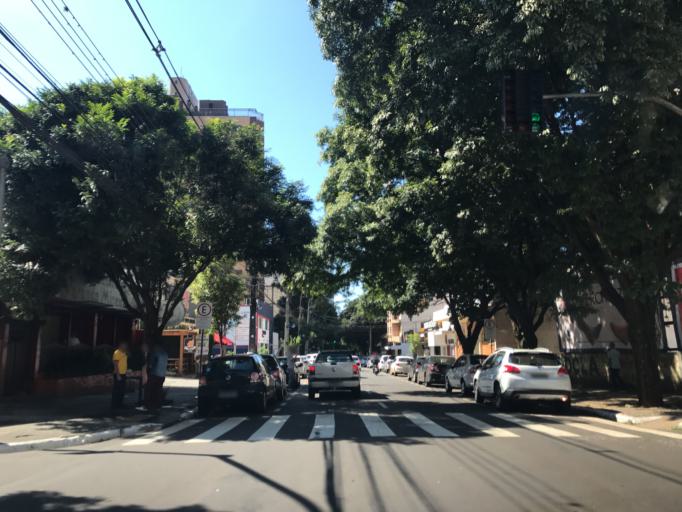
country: BR
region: Parana
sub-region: Maringa
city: Maringa
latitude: -23.4228
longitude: -51.9349
